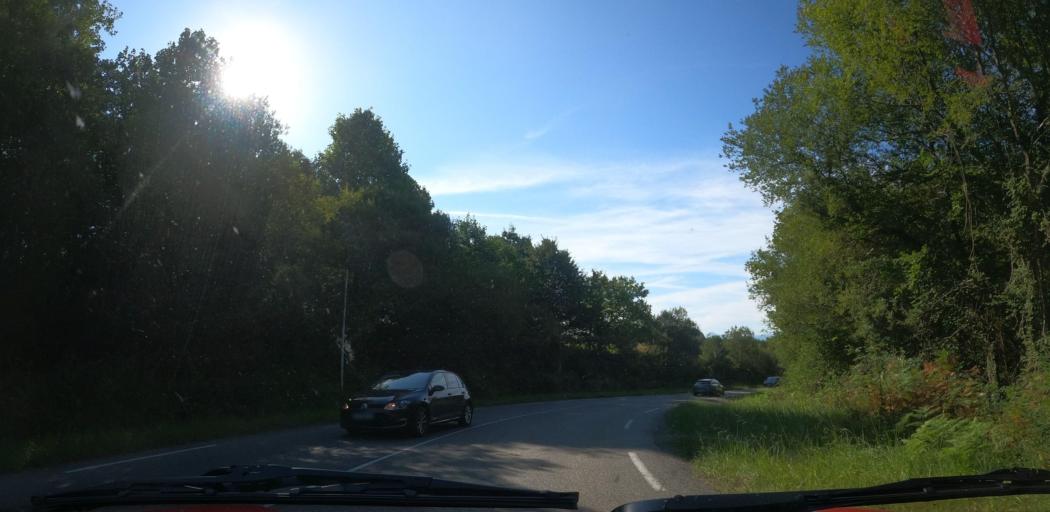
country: FR
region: Aquitaine
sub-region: Departement des Pyrenees-Atlantiques
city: Saint-Pee-sur-Nivelle
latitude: 43.3813
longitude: -1.5394
